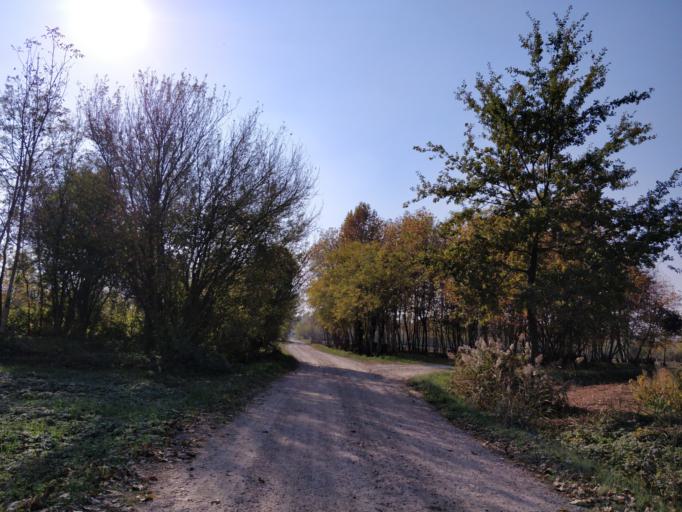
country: IT
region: Friuli Venezia Giulia
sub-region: Provincia di Udine
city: Bertiolo
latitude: 45.9313
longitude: 13.0405
